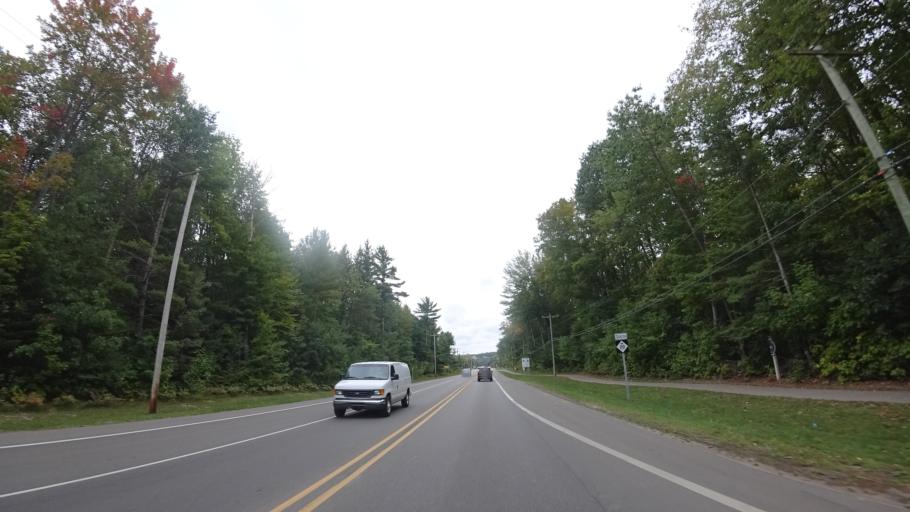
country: US
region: Michigan
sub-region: Emmet County
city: Petoskey
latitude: 45.4079
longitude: -84.9021
